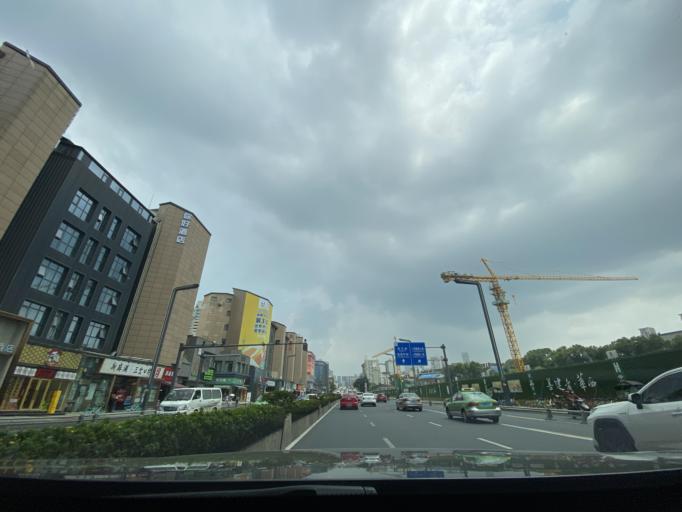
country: CN
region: Sichuan
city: Chengdu
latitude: 30.6332
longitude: 104.0739
